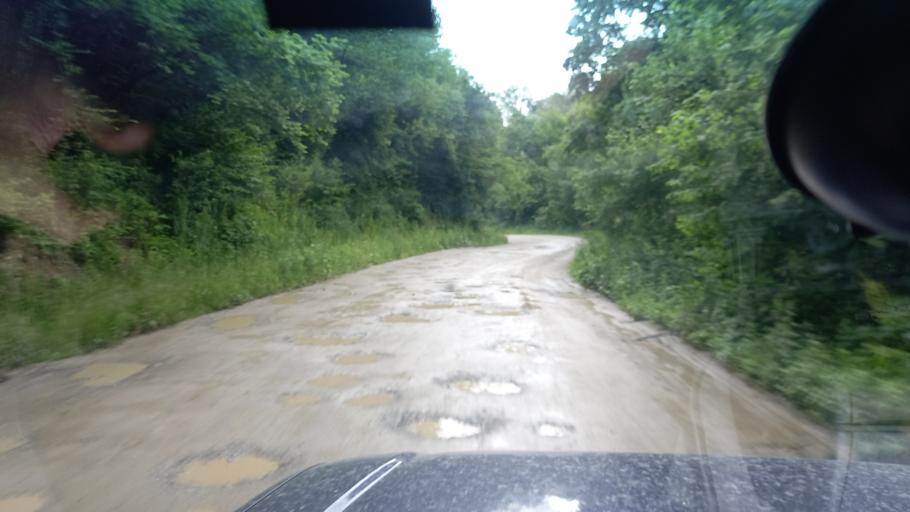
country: RU
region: Krasnodarskiy
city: Psebay
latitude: 44.0319
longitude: 40.7409
